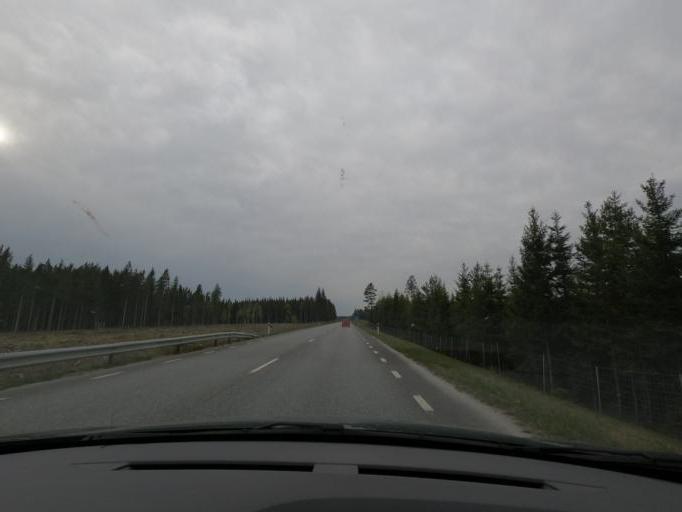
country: SE
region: Vaestra Goetaland
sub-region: Tranemo Kommun
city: Langhem
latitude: 57.5768
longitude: 13.2255
